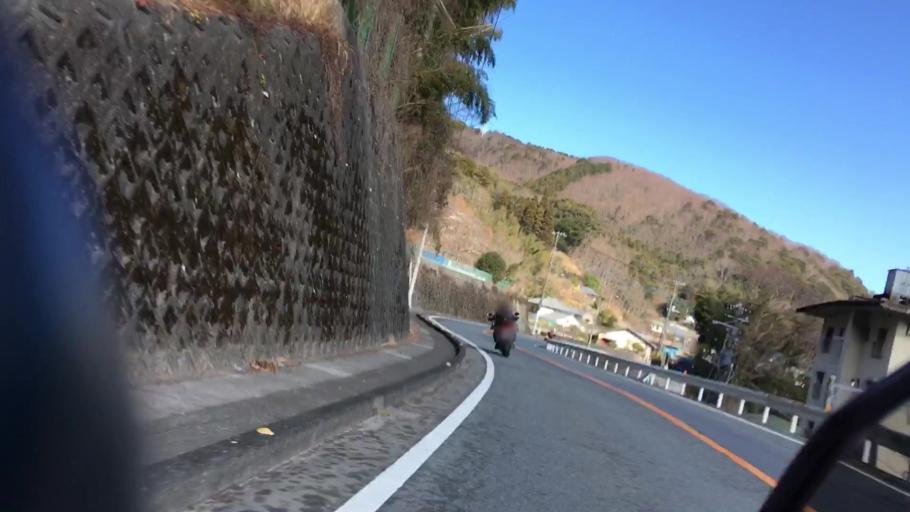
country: JP
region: Shizuoka
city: Heda
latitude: 34.9173
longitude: 138.9044
